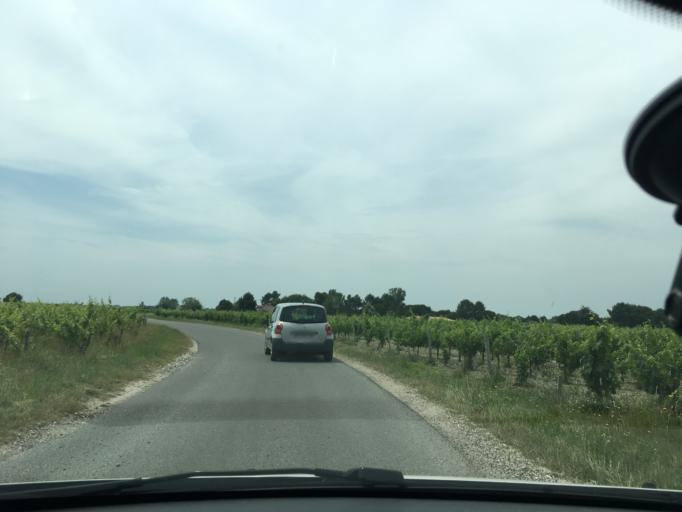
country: FR
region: Aquitaine
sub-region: Departement de la Gironde
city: Listrac-Medoc
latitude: 45.0664
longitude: -0.7978
